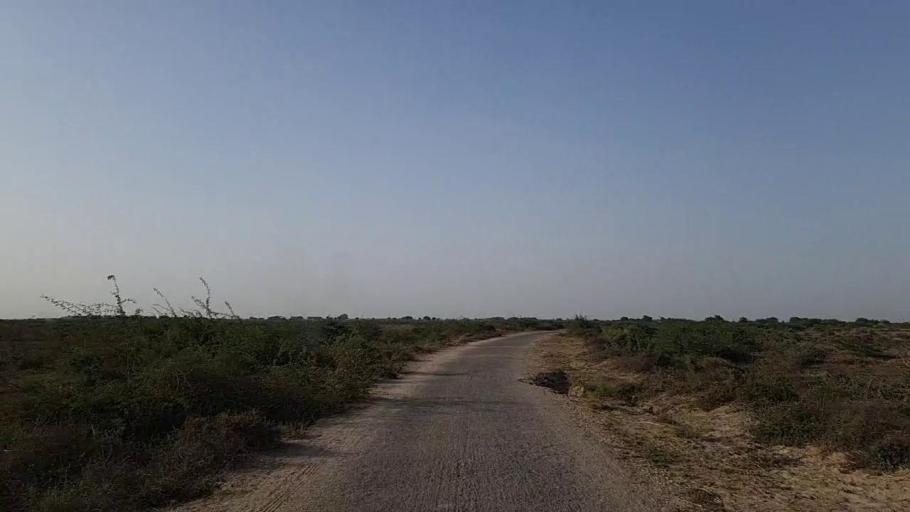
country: PK
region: Sindh
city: Jati
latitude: 24.3060
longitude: 68.1665
